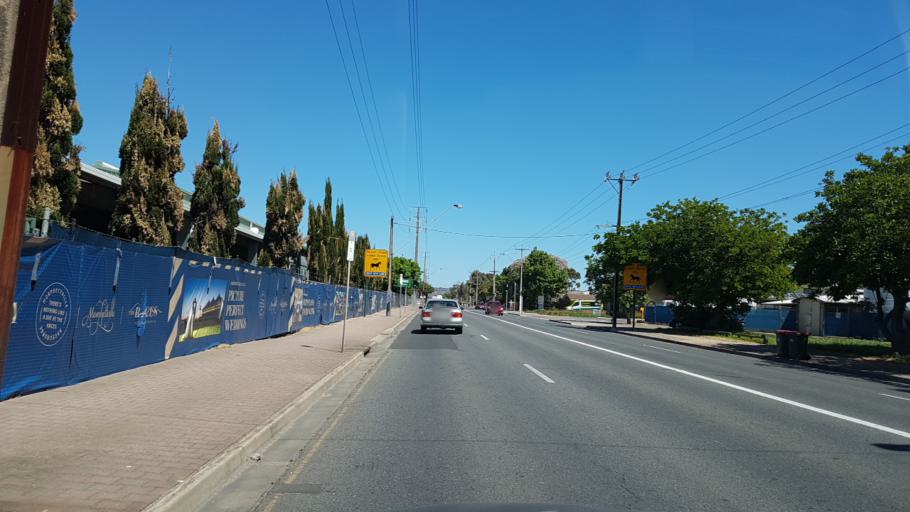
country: AU
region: South Australia
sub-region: Marion
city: Plympton Park
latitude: -34.9795
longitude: 138.5381
